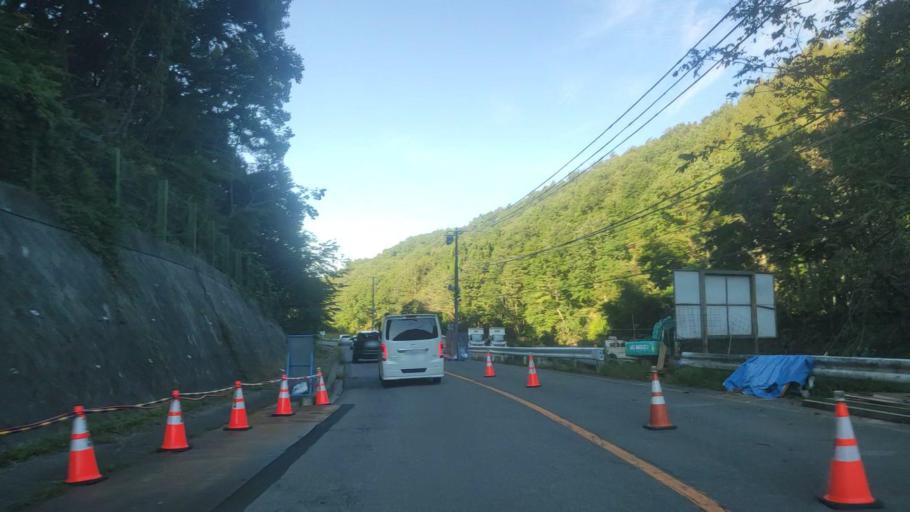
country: JP
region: Nagano
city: Kamimaruko
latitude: 36.2255
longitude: 138.2973
